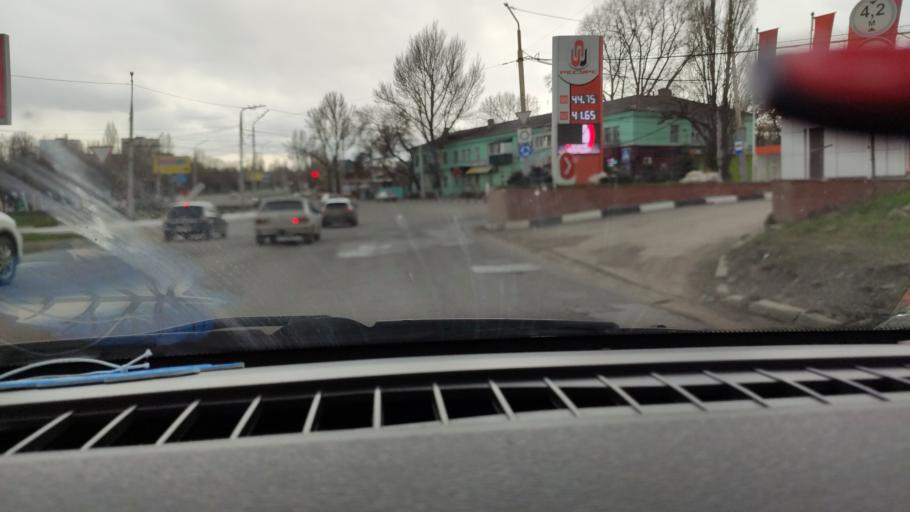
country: RU
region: Saratov
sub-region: Saratovskiy Rayon
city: Saratov
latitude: 51.6151
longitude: 45.9677
